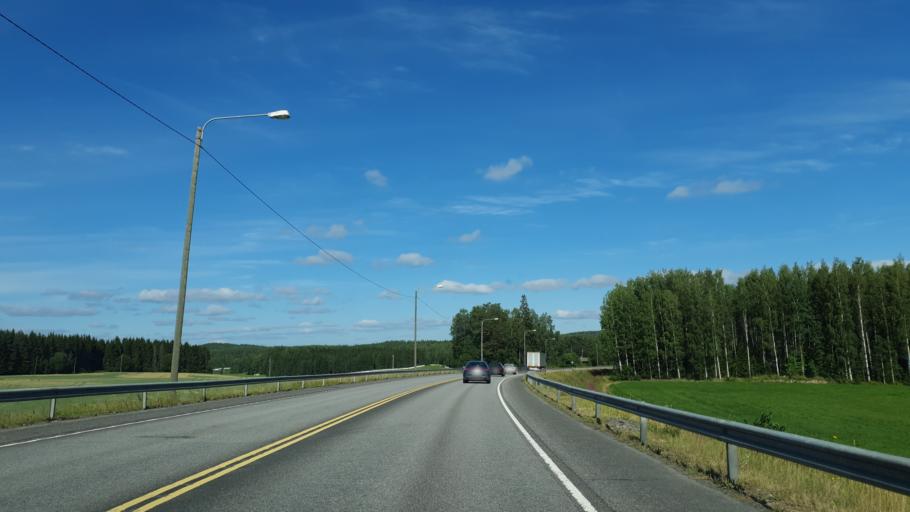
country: FI
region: Central Finland
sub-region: Jyvaeskylae
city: Toivakka
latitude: 62.2434
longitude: 25.9874
